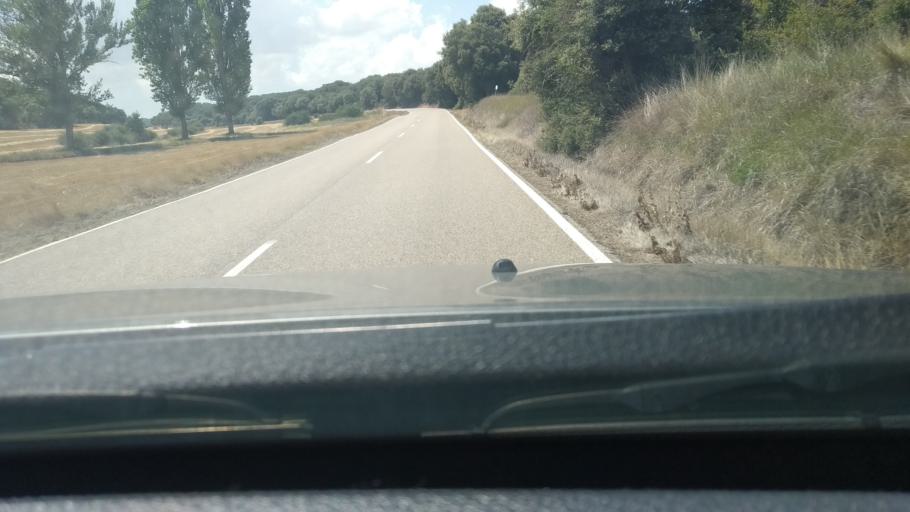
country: ES
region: Castille and Leon
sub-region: Provincia de Burgos
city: Quintanilla de la Mata
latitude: 41.9893
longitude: -3.7759
